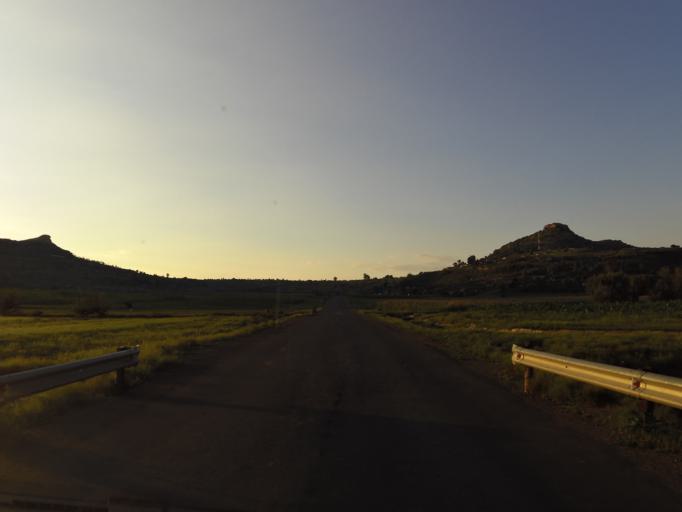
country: LS
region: Leribe
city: Leribe
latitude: -28.8967
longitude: 28.1150
